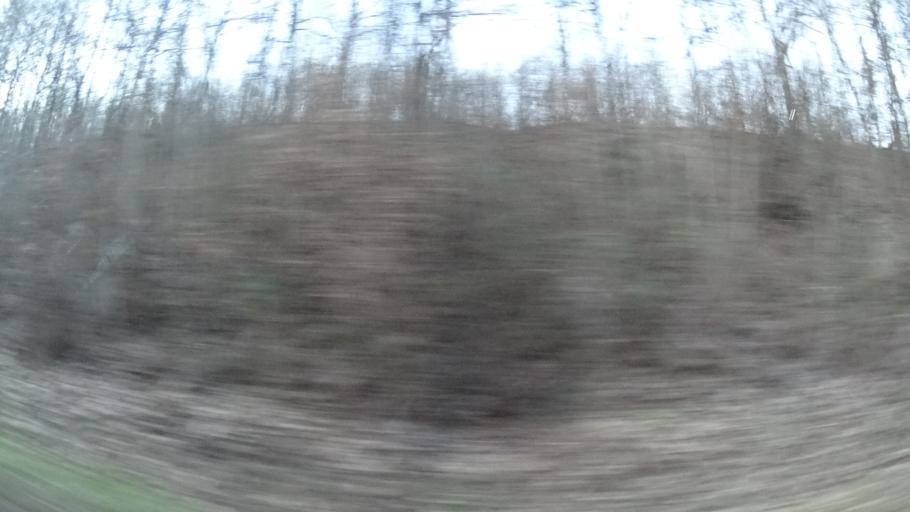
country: DE
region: Bavaria
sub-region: Regierungsbezirk Unterfranken
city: Alzenau in Unterfranken
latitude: 50.0979
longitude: 9.0711
